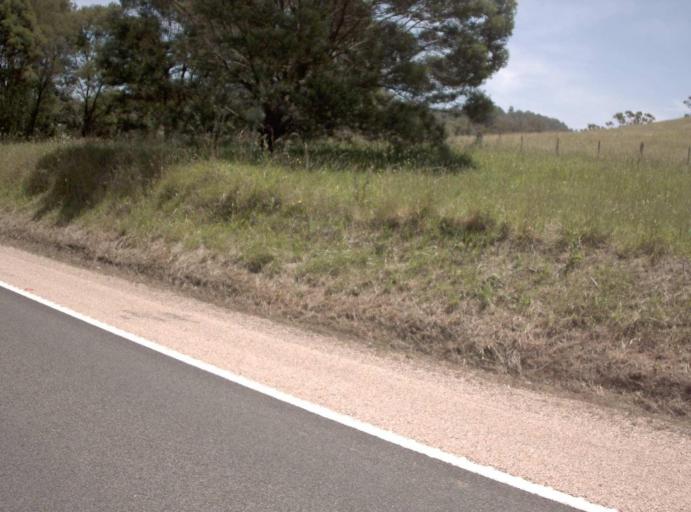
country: AU
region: Victoria
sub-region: East Gippsland
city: Bairnsdale
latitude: -37.7506
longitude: 147.7300
